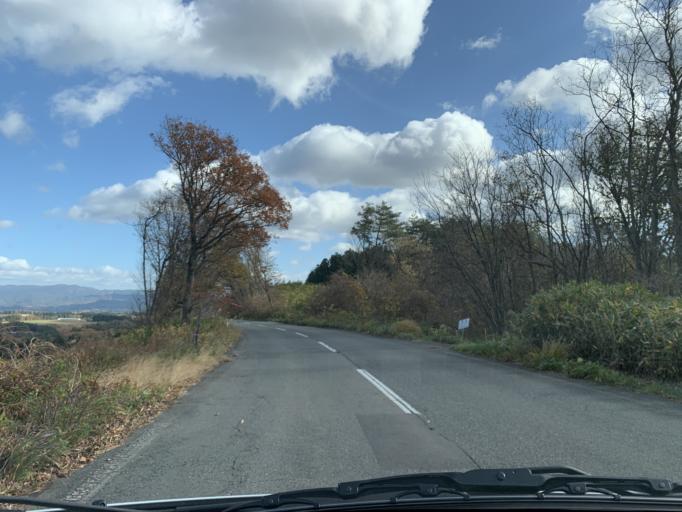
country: JP
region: Iwate
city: Mizusawa
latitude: 39.0446
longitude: 141.0829
